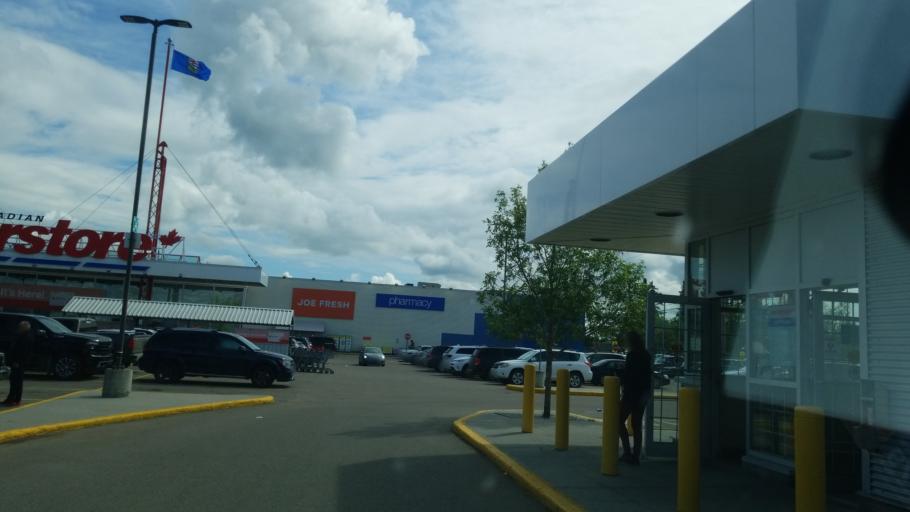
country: CA
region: Saskatchewan
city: Lloydminster
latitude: 53.2768
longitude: -110.0092
